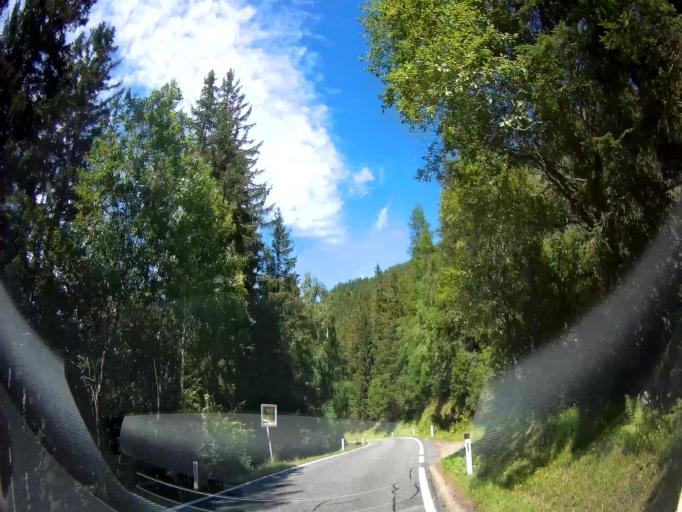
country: AT
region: Carinthia
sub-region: Politischer Bezirk Sankt Veit an der Glan
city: Glodnitz
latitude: 46.9235
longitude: 14.0540
